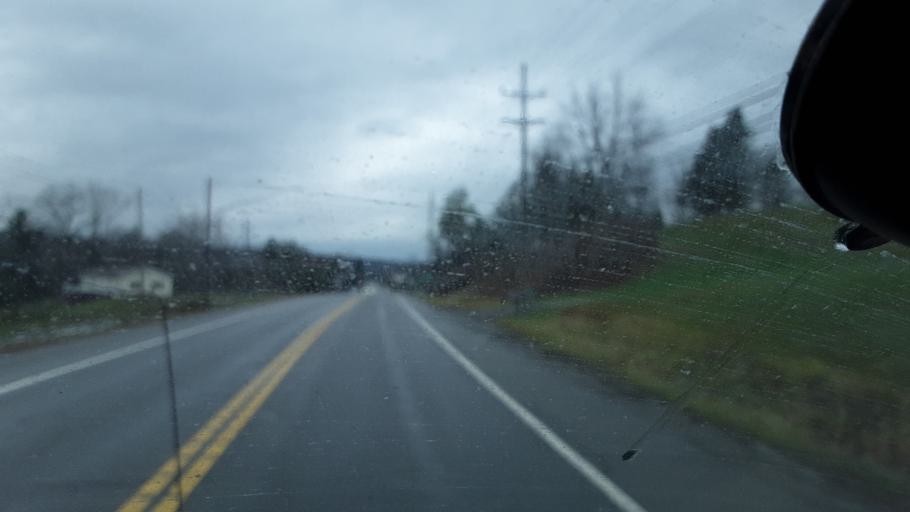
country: US
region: New York
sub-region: Erie County
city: Holland
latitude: 42.6367
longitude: -78.5346
